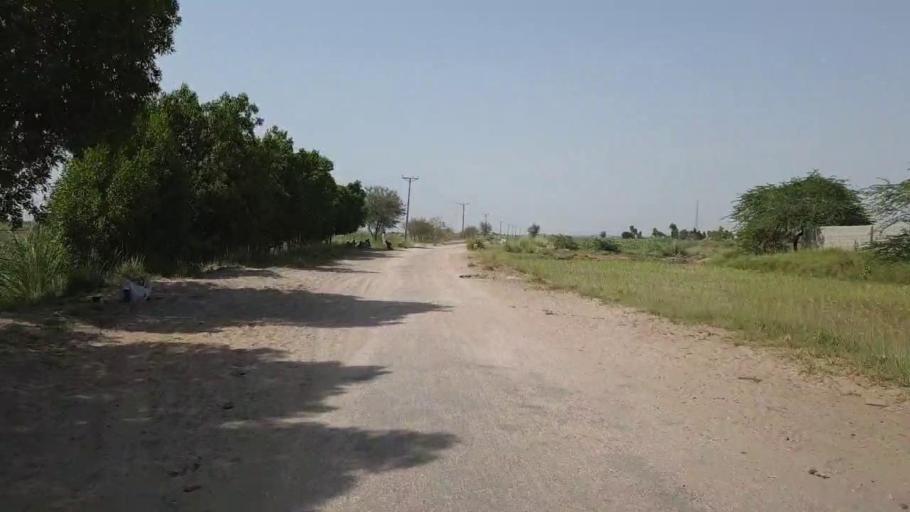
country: PK
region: Sindh
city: Jam Sahib
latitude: 26.4212
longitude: 68.9073
